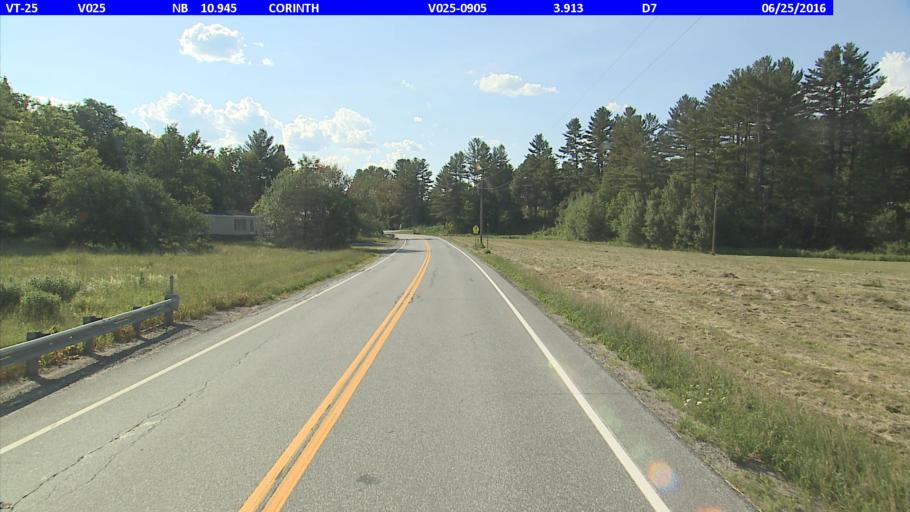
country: US
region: New Hampshire
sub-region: Grafton County
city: Haverhill
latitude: 44.0777
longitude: -72.2600
